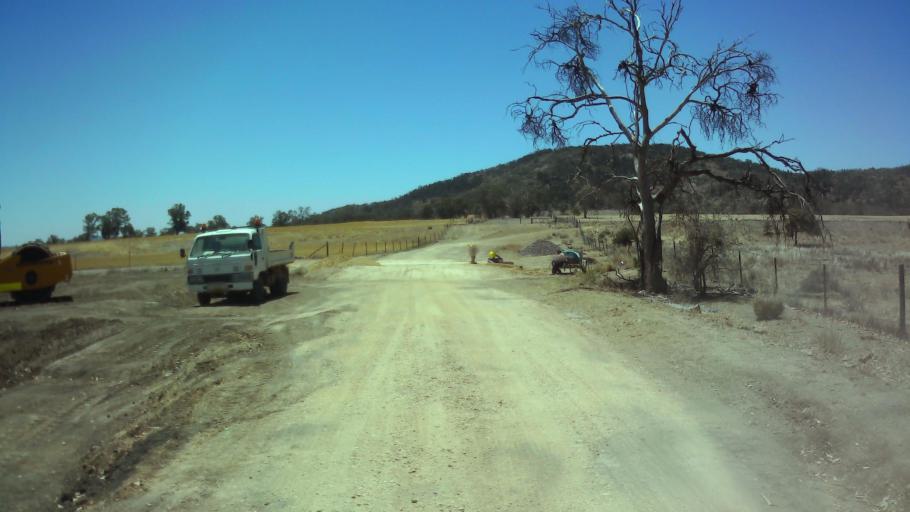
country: AU
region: New South Wales
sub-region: Weddin
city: Grenfell
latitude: -33.8542
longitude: 148.1081
